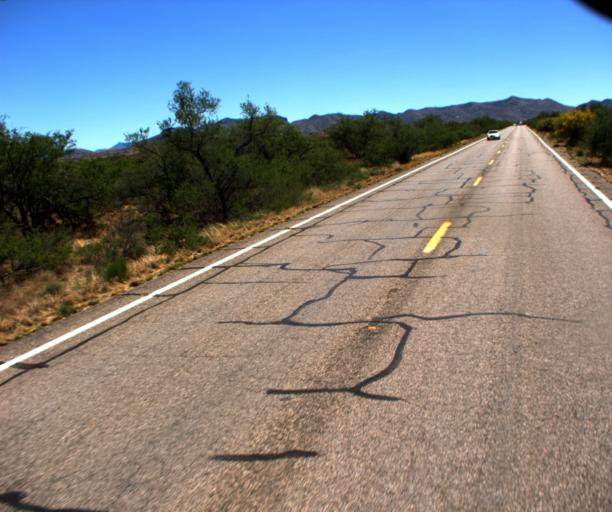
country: US
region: Arizona
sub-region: Pima County
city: Vail
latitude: 31.9681
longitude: -110.6740
